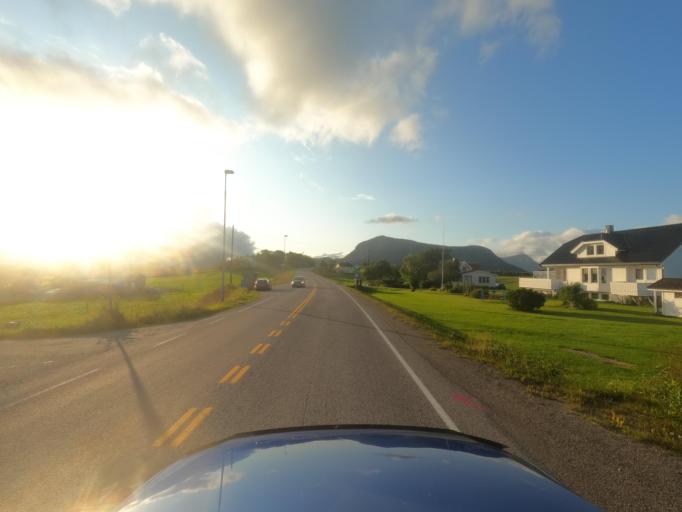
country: NO
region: Nordland
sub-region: Vestvagoy
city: Gravdal
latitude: 68.1363
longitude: 13.5606
